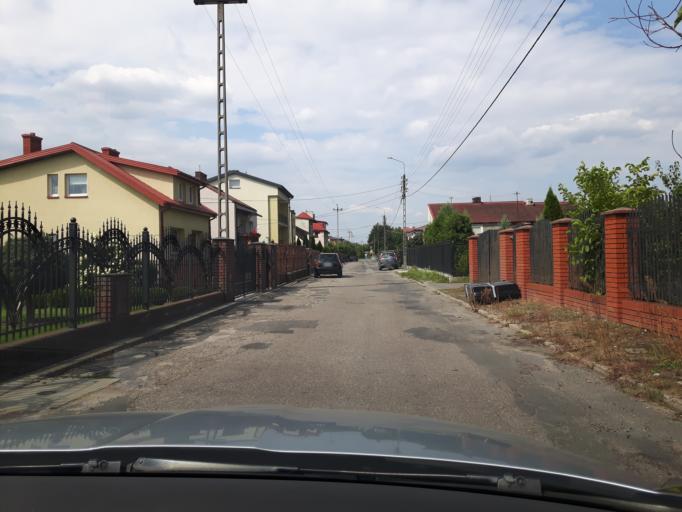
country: PL
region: Masovian Voivodeship
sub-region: Powiat wolominski
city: Zabki
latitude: 52.2991
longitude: 21.1060
